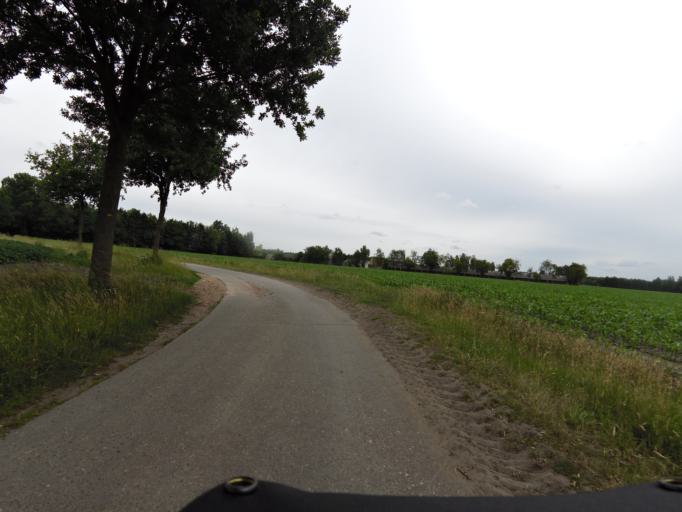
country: NL
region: North Brabant
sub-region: Gemeente Goirle
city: Goirle
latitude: 51.4578
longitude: 5.0711
